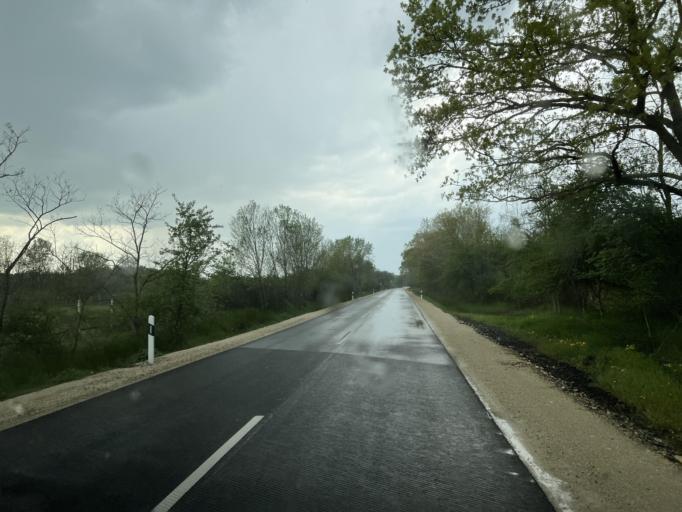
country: HU
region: Pest
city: Csemo
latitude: 47.0777
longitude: 19.6800
